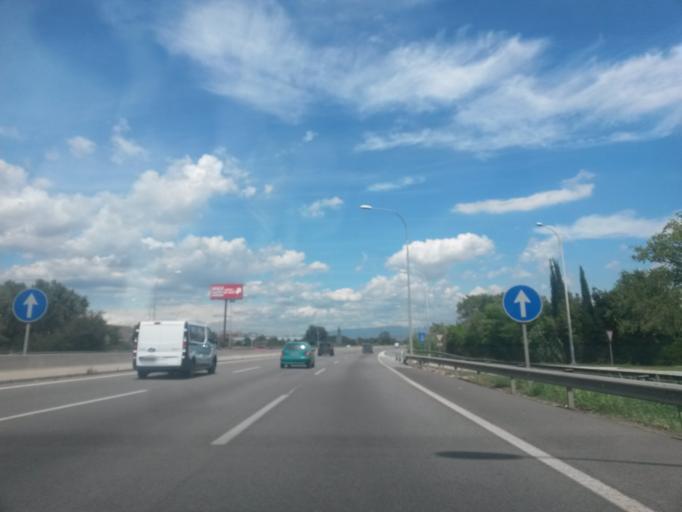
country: ES
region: Catalonia
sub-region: Provincia de Barcelona
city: Montcada i Reixac
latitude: 41.4966
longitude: 2.1915
